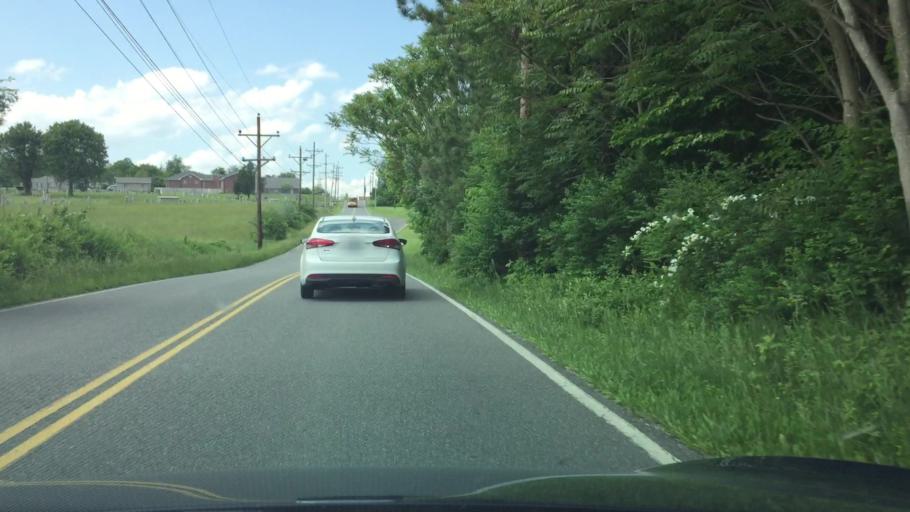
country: US
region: Virginia
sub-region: Pulaski County
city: Dublin
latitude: 37.0827
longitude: -80.6831
